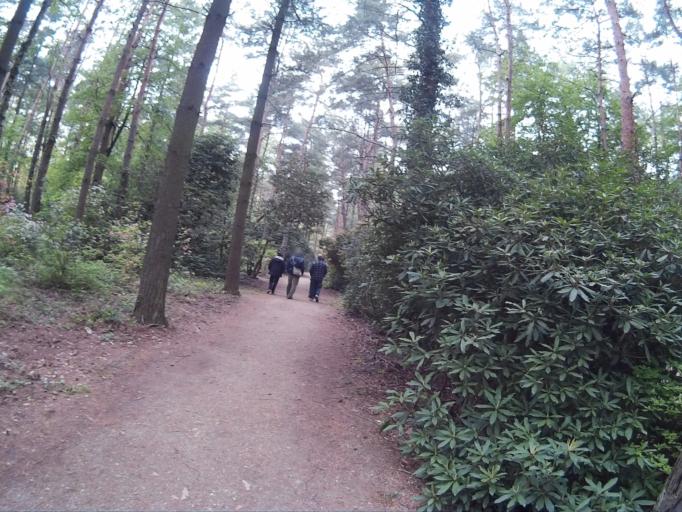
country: HU
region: Vas
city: Vasvar
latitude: 47.0730
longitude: 16.8922
